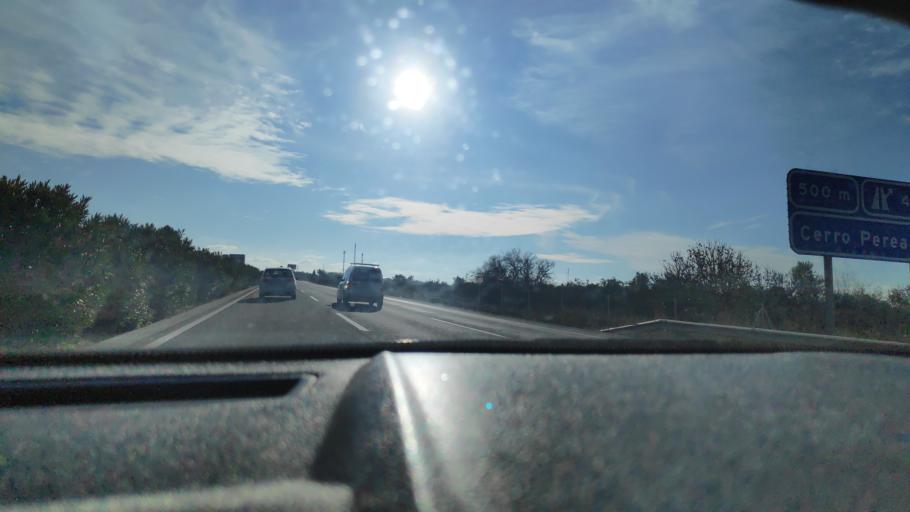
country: ES
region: Andalusia
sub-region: Province of Cordoba
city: La Carlota
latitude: 37.5967
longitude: -4.9762
